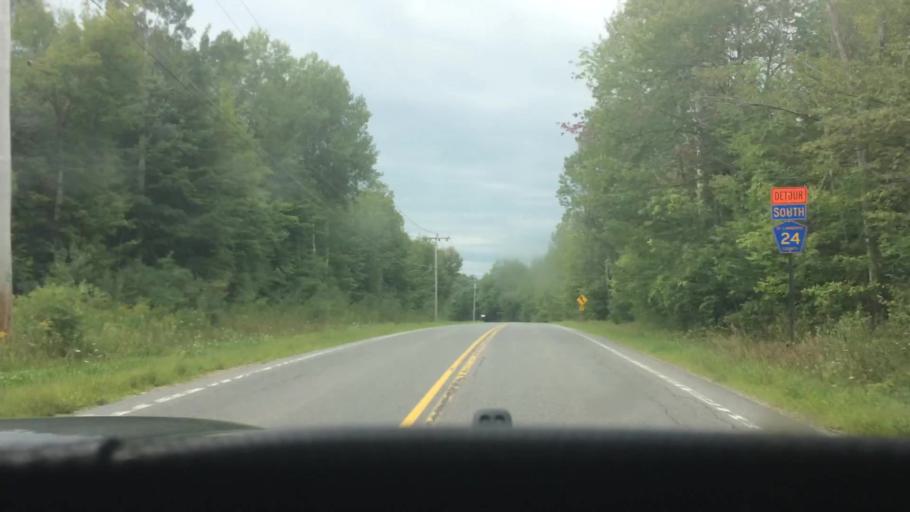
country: US
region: New York
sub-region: St. Lawrence County
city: Canton
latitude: 44.5159
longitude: -75.2007
